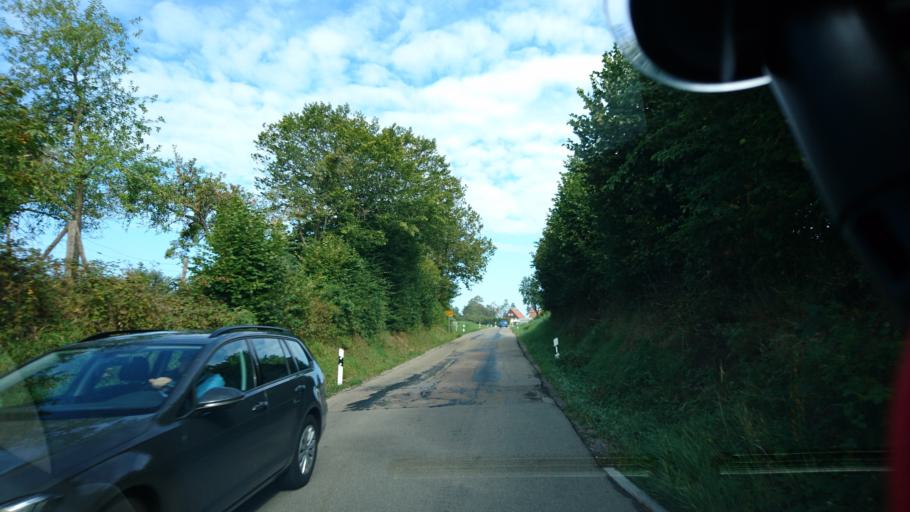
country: DE
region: Baden-Wuerttemberg
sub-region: Regierungsbezirk Stuttgart
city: Mainhardt
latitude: 49.0937
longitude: 9.5576
